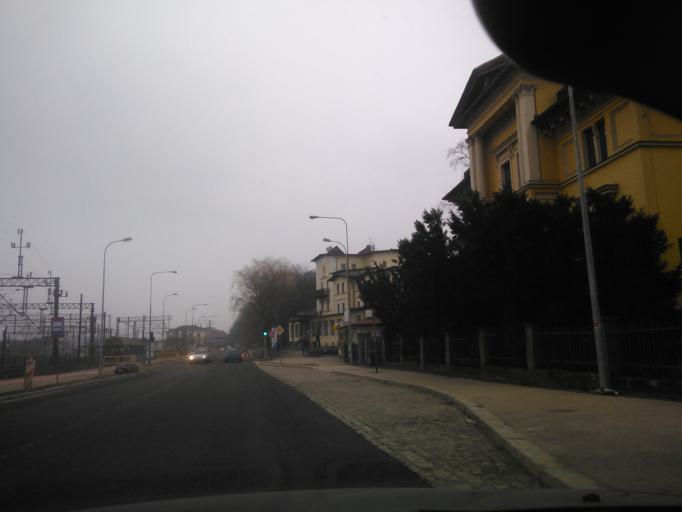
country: PL
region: Lower Silesian Voivodeship
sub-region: Jelenia Gora
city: Jelenia Gora
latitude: 50.9031
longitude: 15.7506
